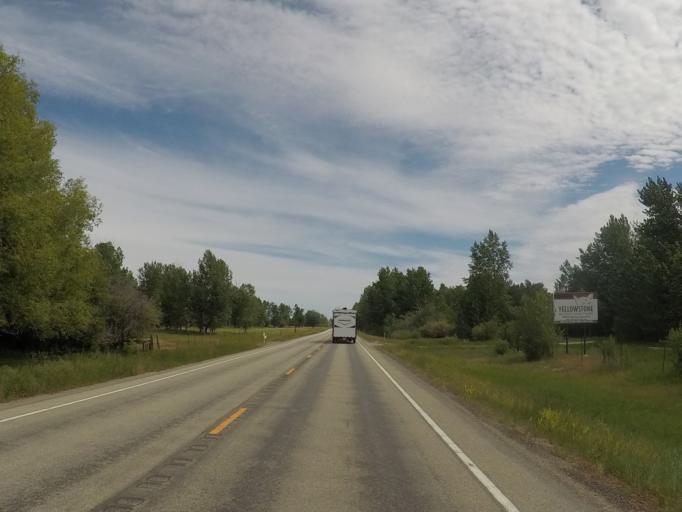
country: US
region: Montana
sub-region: Carbon County
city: Red Lodge
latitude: 45.2700
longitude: -109.2216
